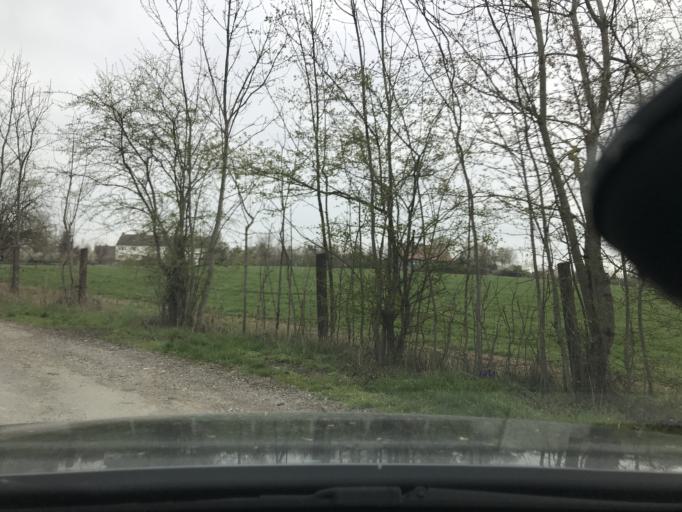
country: DE
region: Thuringia
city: Muehlhausen
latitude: 51.2239
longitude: 10.4243
